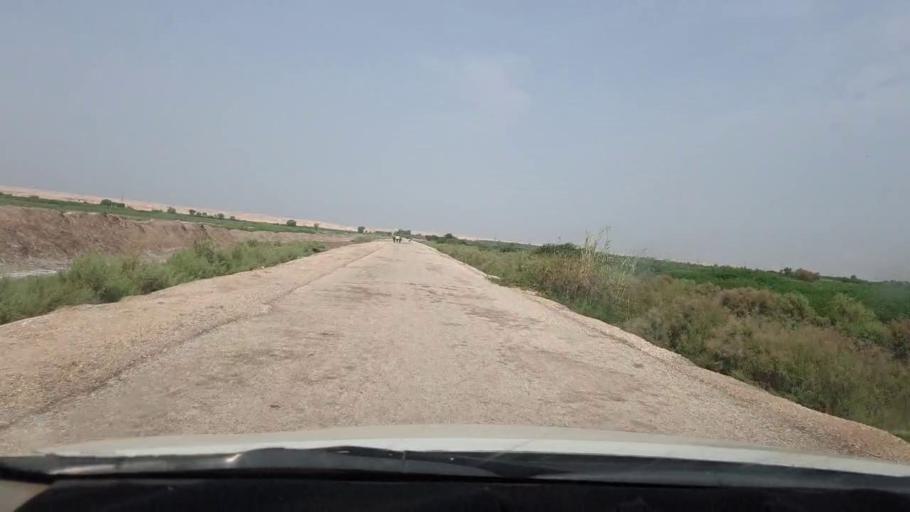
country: PK
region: Sindh
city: Rohri
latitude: 27.5950
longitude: 68.9970
